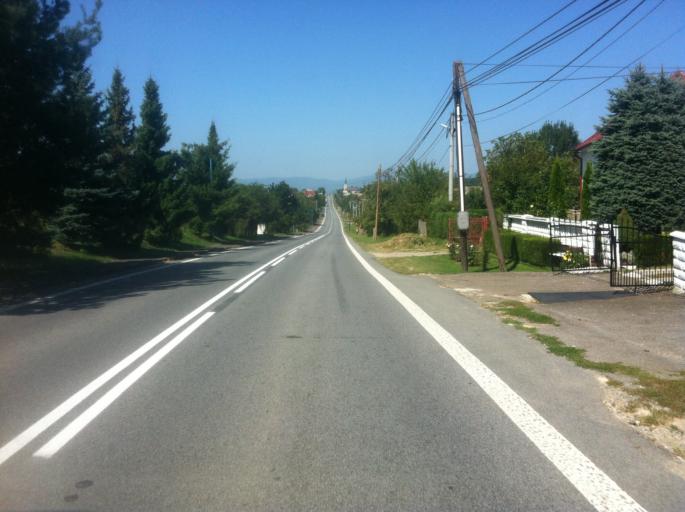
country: SK
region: Kosicky
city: Sobrance
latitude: 48.7022
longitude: 22.2282
